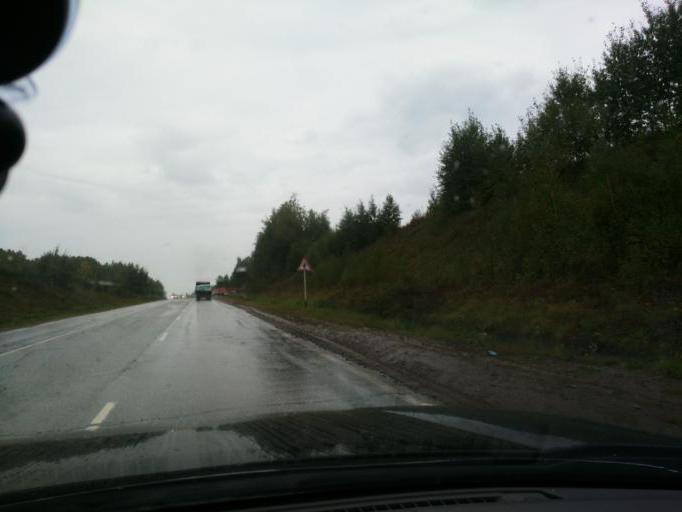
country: RU
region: Perm
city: Yugo-Kamskiy
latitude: 57.4947
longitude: 55.6861
